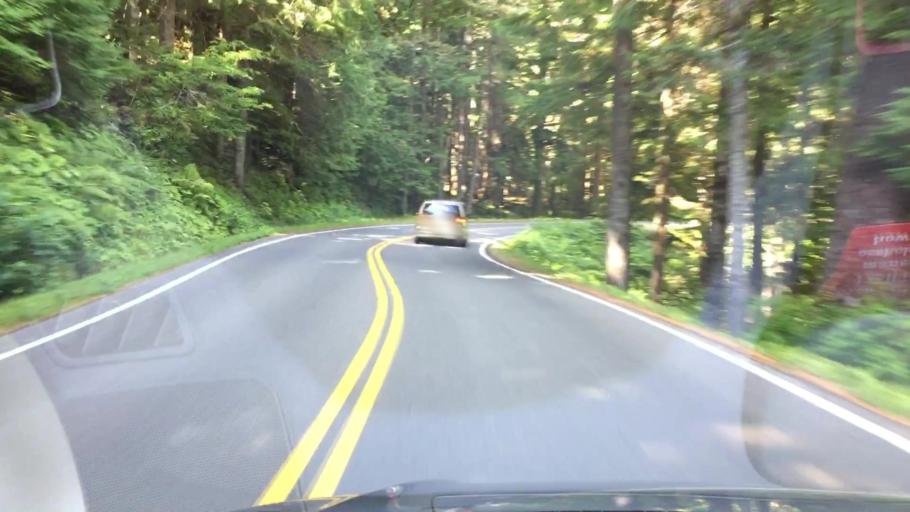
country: US
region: Washington
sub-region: Pierce County
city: Eatonville
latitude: 46.7339
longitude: -121.8314
